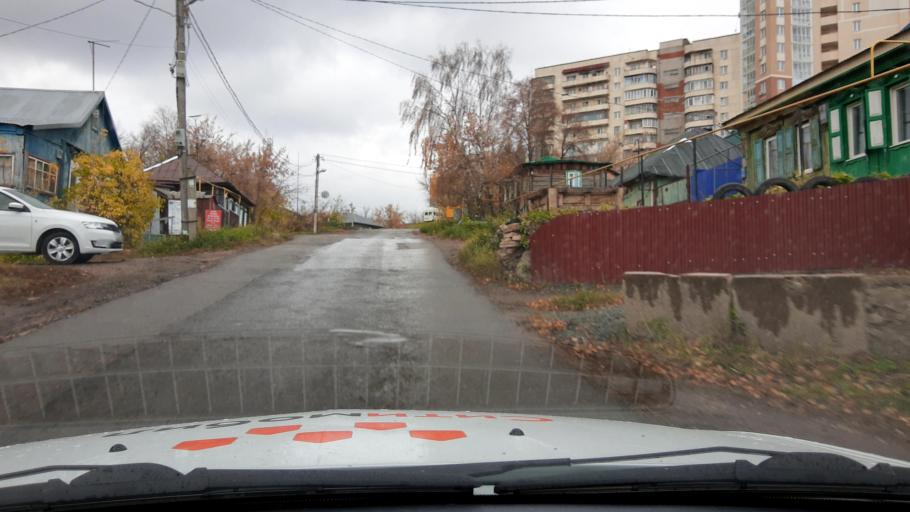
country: RU
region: Bashkortostan
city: Ufa
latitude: 54.7391
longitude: 55.9329
